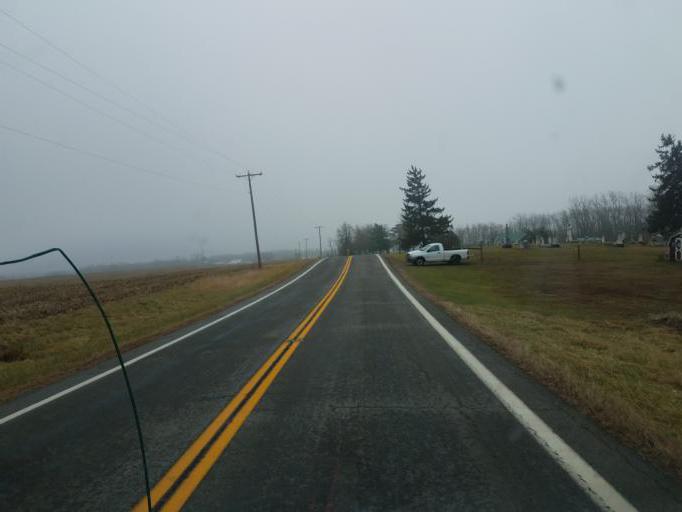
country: US
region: Ohio
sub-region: Champaign County
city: North Lewisburg
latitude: 40.2631
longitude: -83.5881
